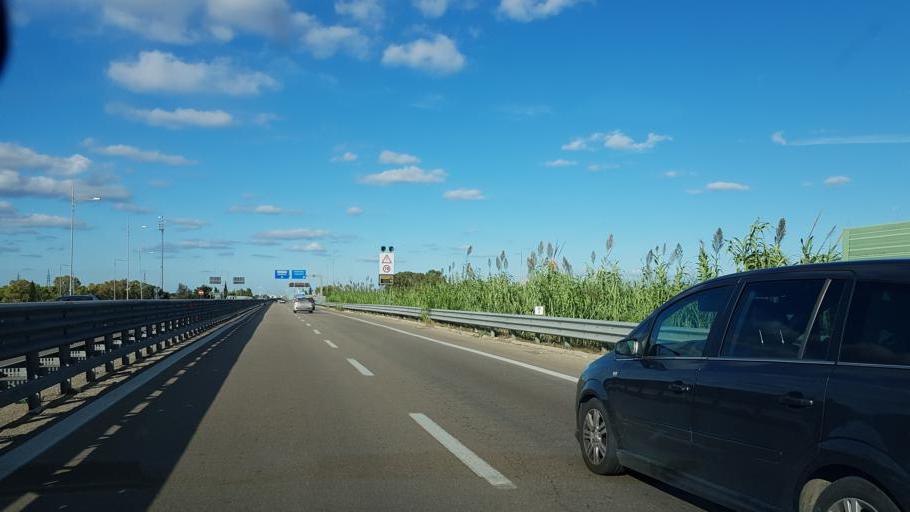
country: IT
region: Apulia
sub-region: Provincia di Lecce
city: Giorgilorio
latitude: 40.3616
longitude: 18.1420
